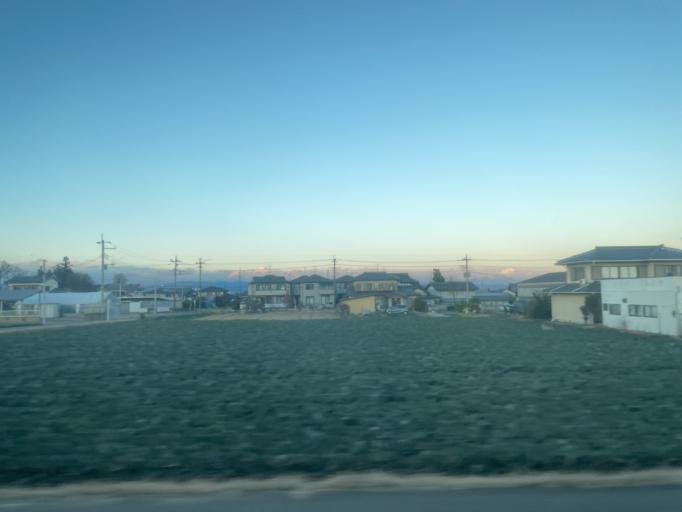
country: JP
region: Saitama
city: Fukayacho
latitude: 36.1987
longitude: 139.2538
